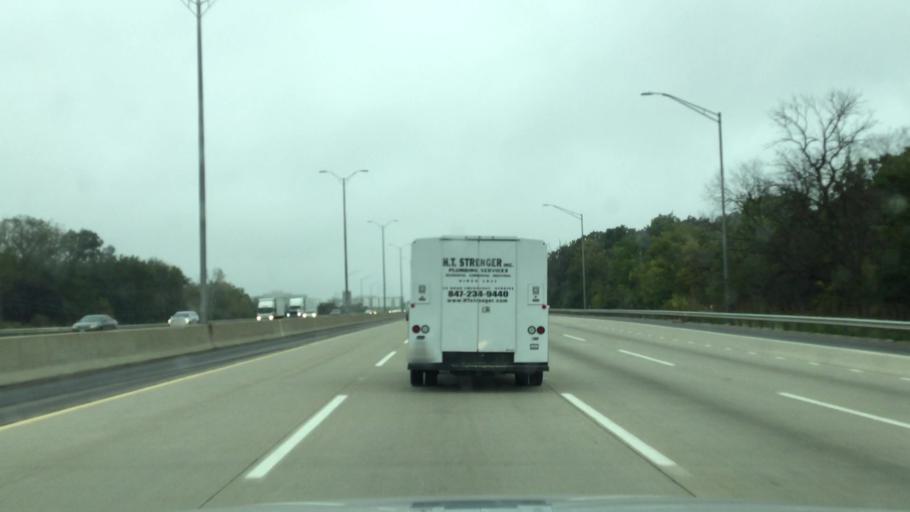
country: US
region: Illinois
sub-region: Lake County
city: Lincolnshire
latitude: 42.2307
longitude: -87.9013
